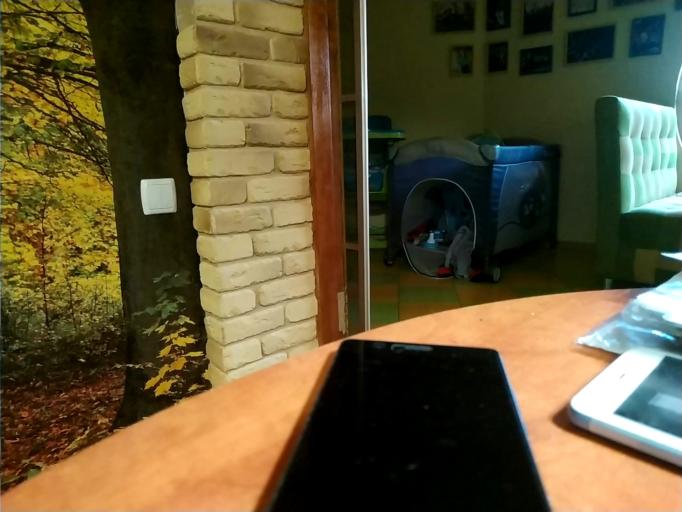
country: RU
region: Orjol
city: Znamenskoye
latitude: 53.5829
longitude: 35.4759
